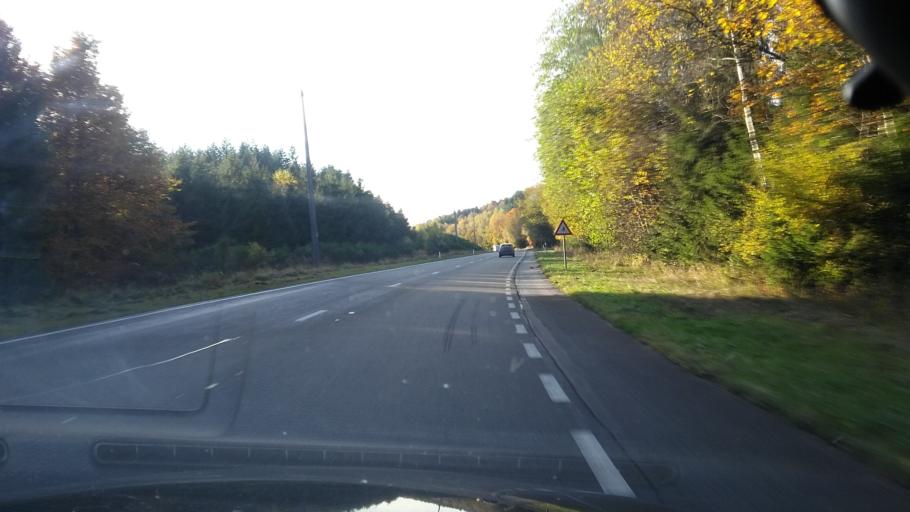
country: BE
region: Wallonia
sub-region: Province du Luxembourg
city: Bouillon
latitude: 49.7622
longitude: 5.1206
